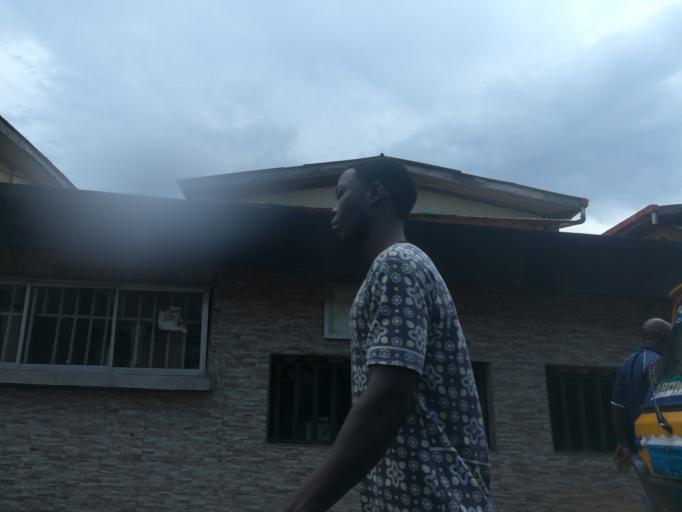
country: NG
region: Lagos
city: Ojota
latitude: 6.5639
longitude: 3.3701
